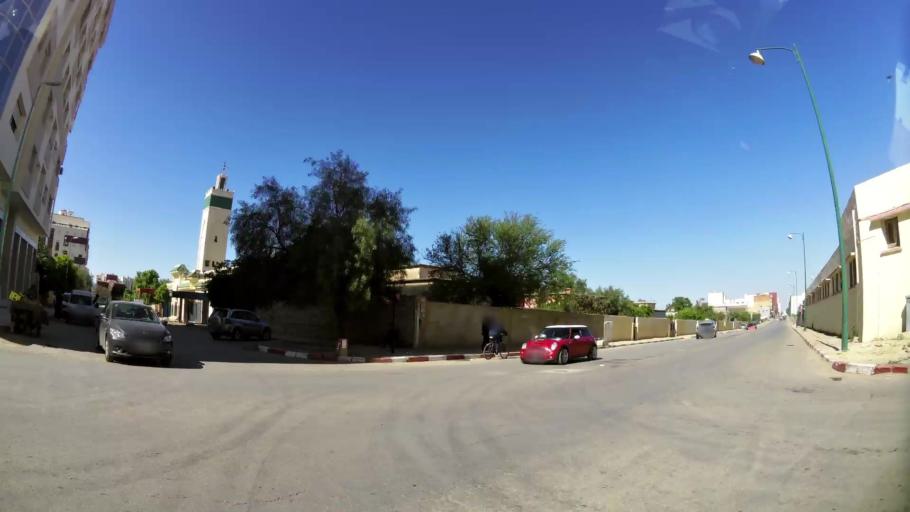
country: MA
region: Meknes-Tafilalet
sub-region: Meknes
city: Meknes
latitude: 33.8927
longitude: -5.5278
